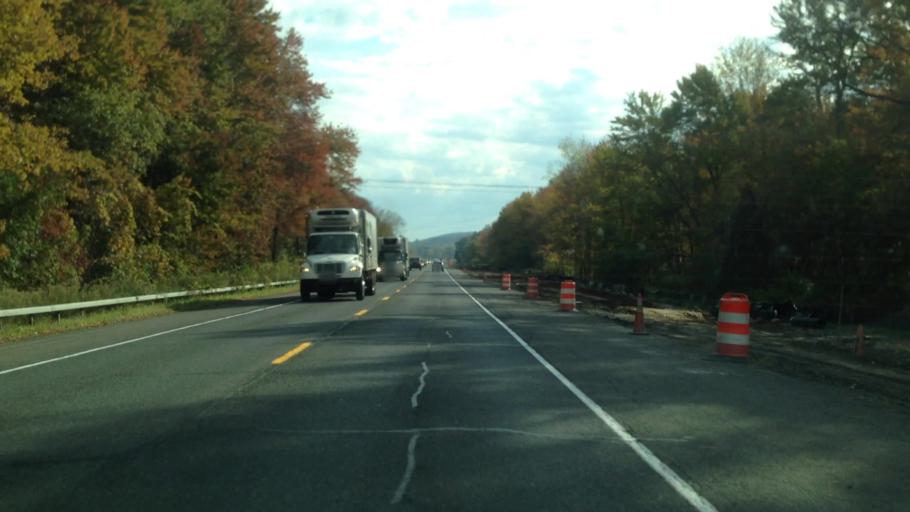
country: US
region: New York
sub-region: Ulster County
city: New Paltz
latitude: 41.7395
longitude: -74.0492
